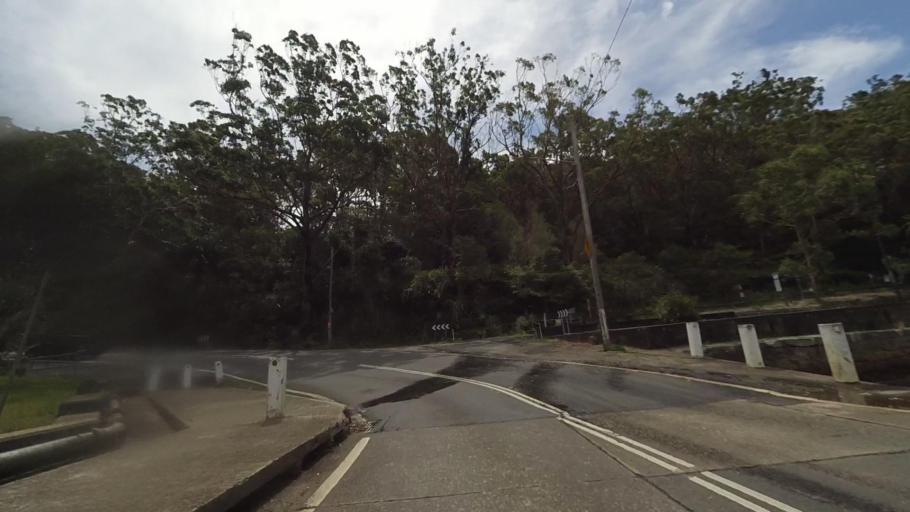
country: AU
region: New South Wales
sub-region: Sutherland Shire
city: Loftus
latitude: -34.0732
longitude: 151.0569
